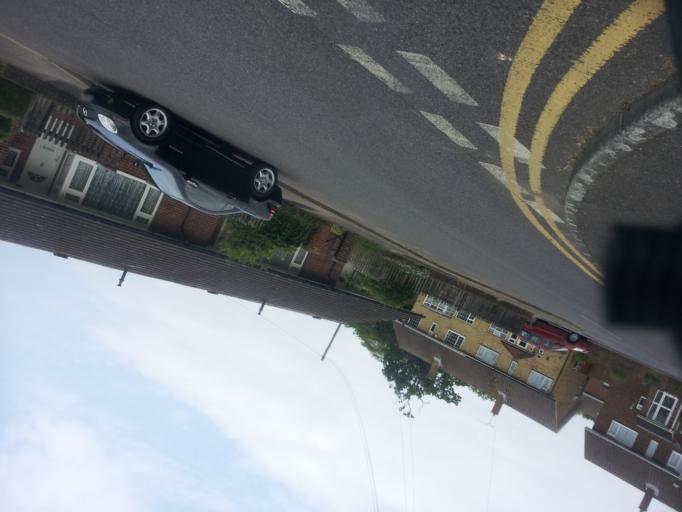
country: GB
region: England
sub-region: Kent
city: Larkfield
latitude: 51.2957
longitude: 0.4375
